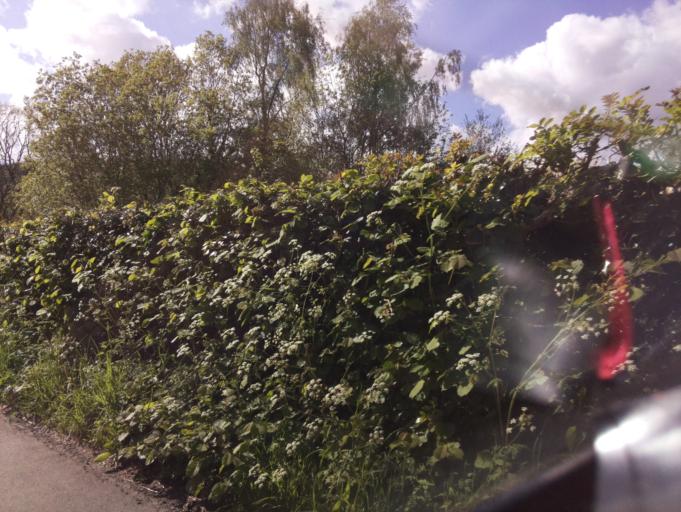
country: GB
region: Wales
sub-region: Caerphilly County Borough
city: Machen
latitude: 51.5795
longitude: -3.1232
